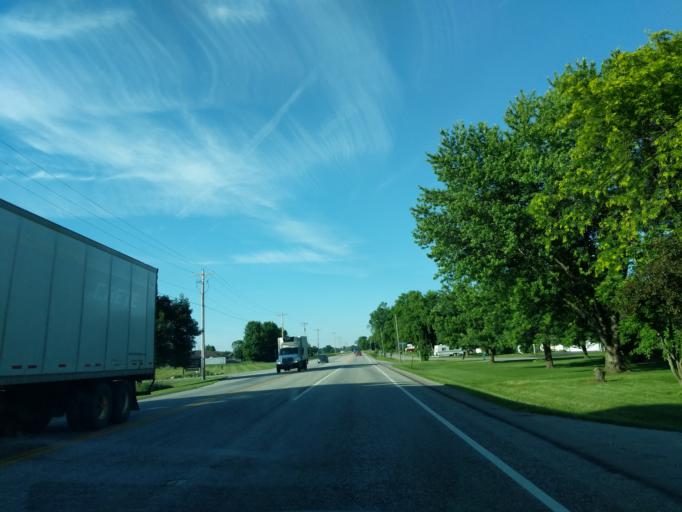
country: US
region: Indiana
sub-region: Madison County
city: Pendleton
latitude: 39.9777
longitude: -85.7543
